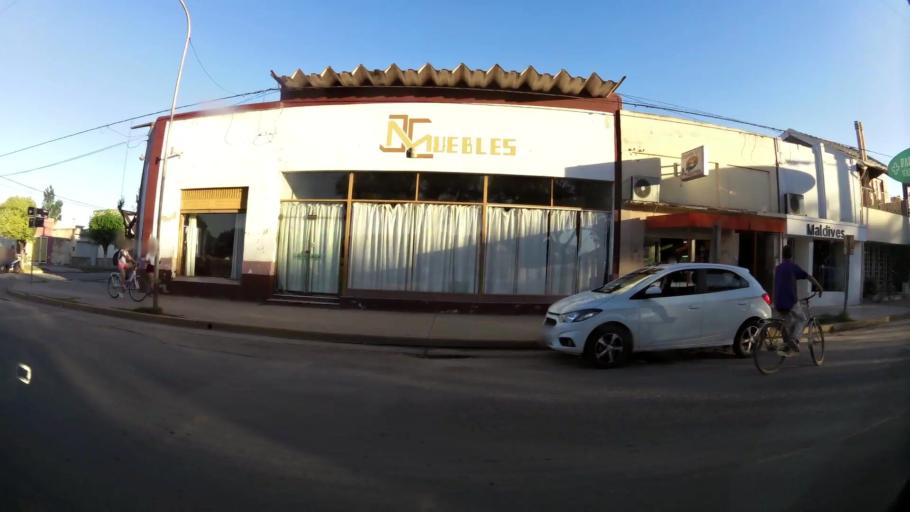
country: AR
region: Cordoba
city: Pozo del Molle
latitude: -32.0199
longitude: -62.9203
